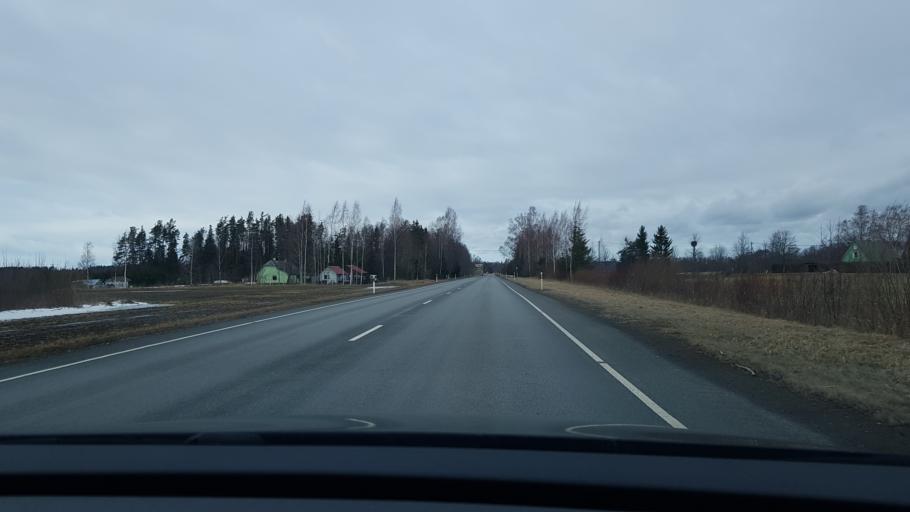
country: EE
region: Paernumaa
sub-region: Paikuse vald
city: Paikuse
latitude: 58.2263
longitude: 24.7026
